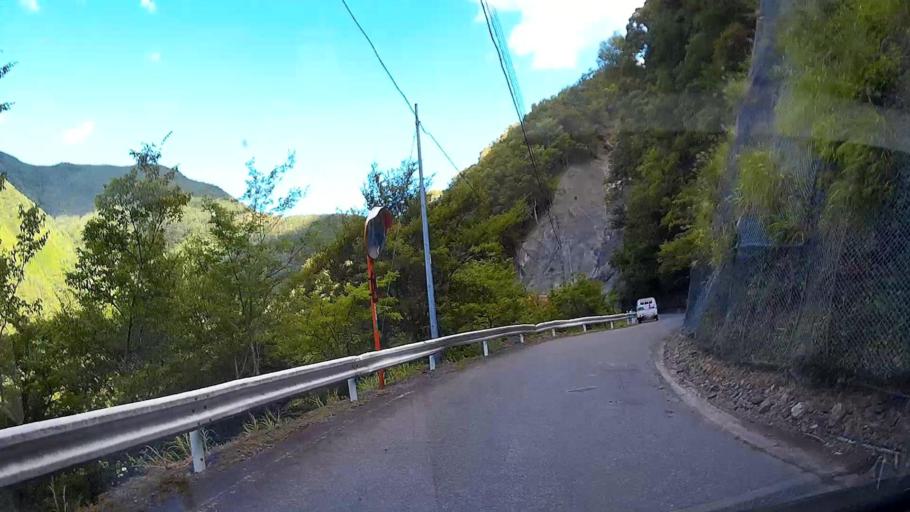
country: JP
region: Shizuoka
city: Shizuoka-shi
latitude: 35.2862
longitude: 138.2193
